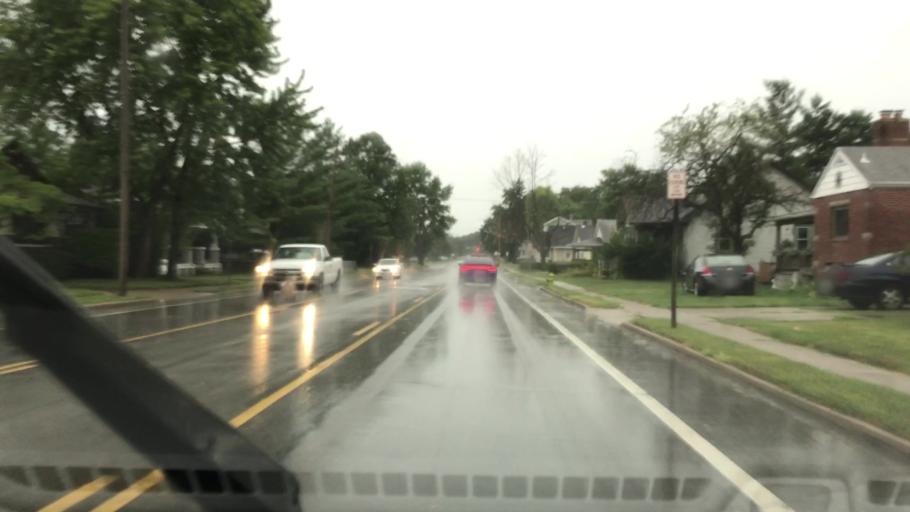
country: US
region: Ohio
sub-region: Greene County
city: Fairborn
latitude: 39.8196
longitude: -84.0260
